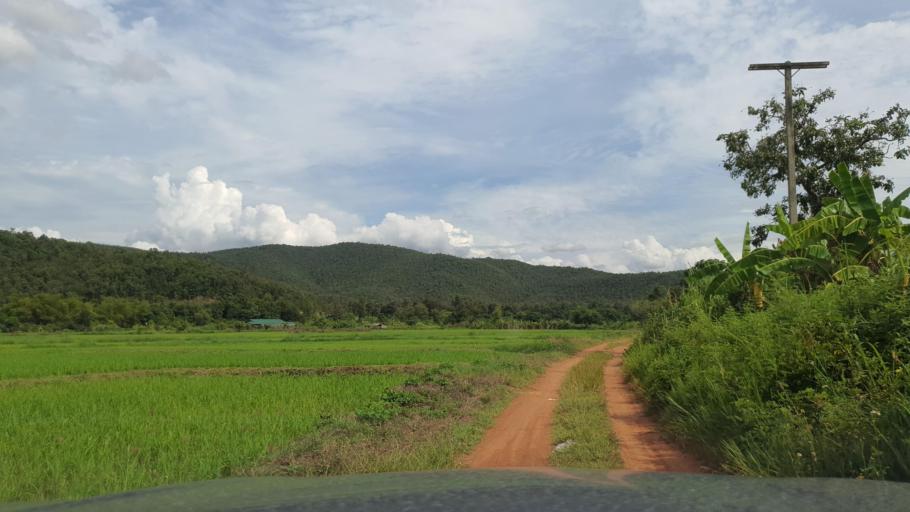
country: TH
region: Chiang Mai
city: Mae On
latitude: 18.7813
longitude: 99.1868
